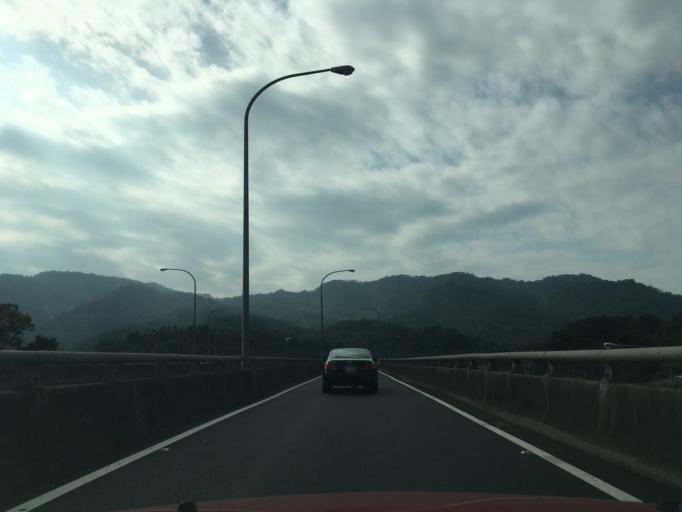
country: TW
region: Taipei
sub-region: Taipei
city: Banqiao
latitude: 24.9633
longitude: 121.4325
